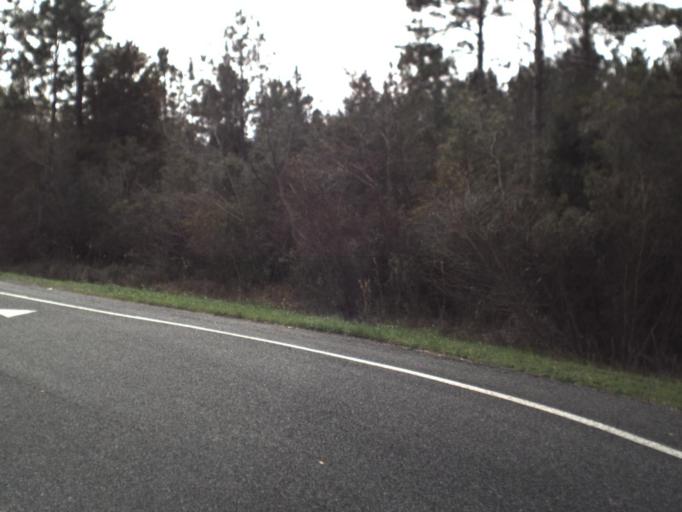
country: US
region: Florida
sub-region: Bay County
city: Youngstown
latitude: 30.5937
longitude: -85.3960
